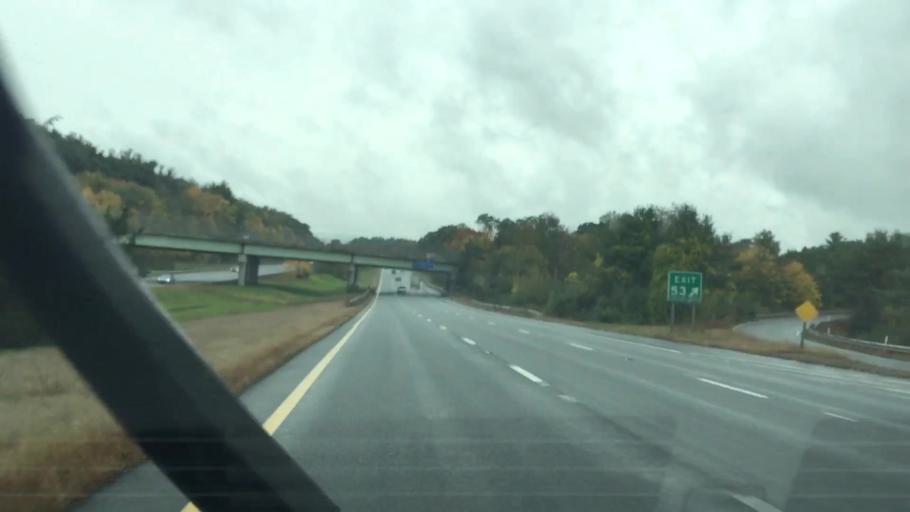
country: US
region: Massachusetts
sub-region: Essex County
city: Merrimac
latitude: 42.8311
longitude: -70.9895
